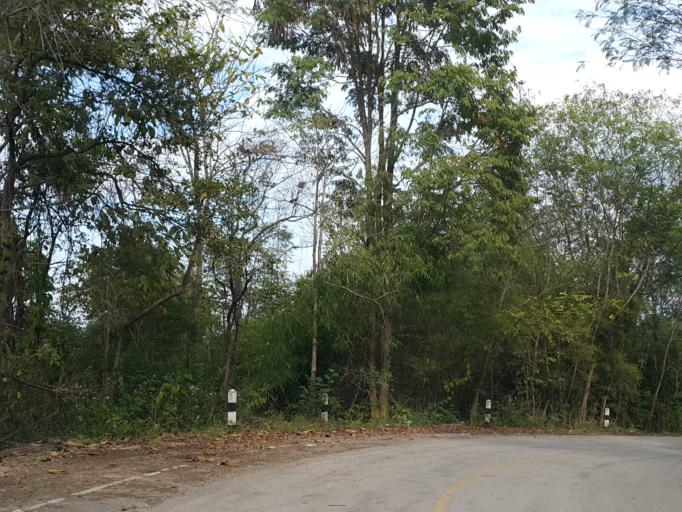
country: TH
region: Lampang
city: Chae Hom
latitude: 18.6539
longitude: 99.5295
